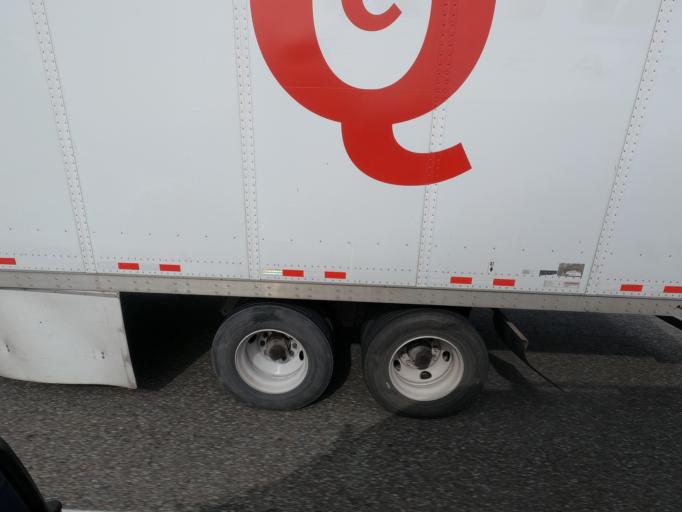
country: US
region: Tennessee
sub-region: Henderson County
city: Lexington
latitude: 35.7760
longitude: -88.4303
